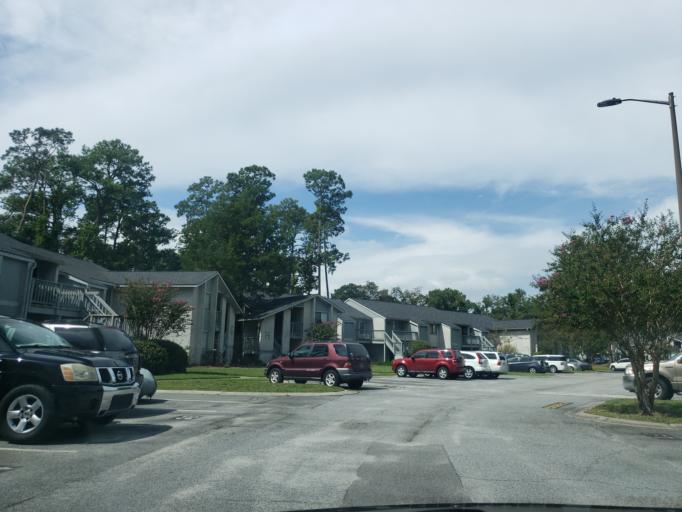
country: US
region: Georgia
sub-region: Chatham County
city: Wilmington Island
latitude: 32.0262
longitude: -80.9641
